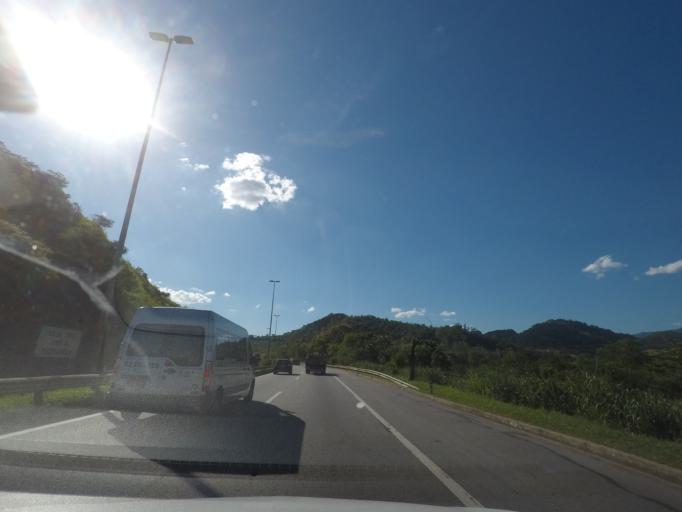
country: BR
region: Rio de Janeiro
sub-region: Petropolis
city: Petropolis
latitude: -22.6565
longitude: -43.1208
